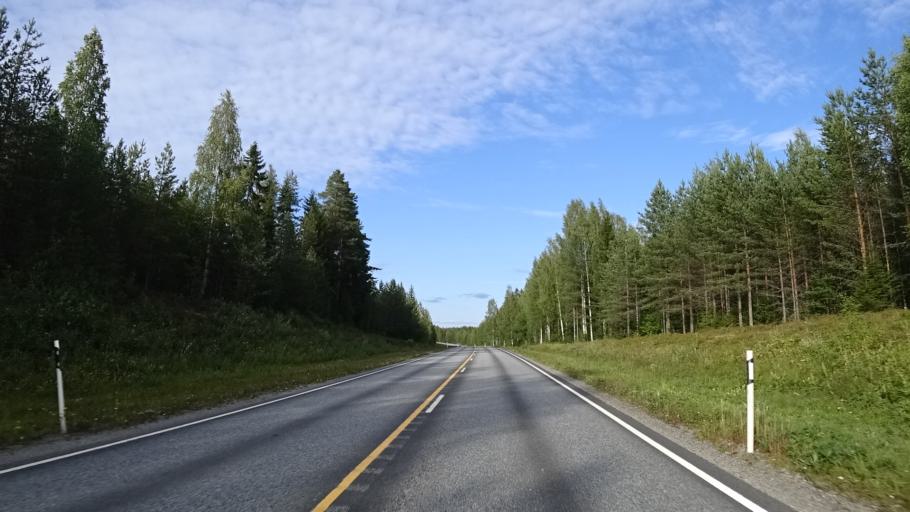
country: FI
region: North Karelia
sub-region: Joensuu
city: Eno
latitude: 62.8136
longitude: 30.1765
